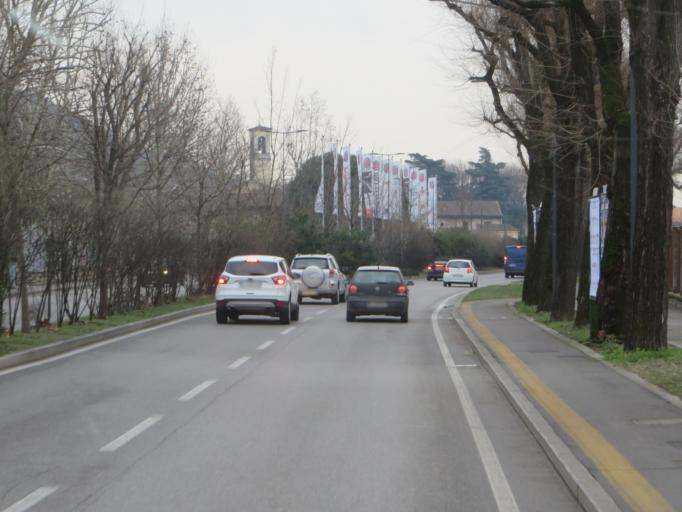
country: IT
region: Lombardy
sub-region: Provincia di Brescia
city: Buffalora-Bettole
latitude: 45.5258
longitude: 10.2637
